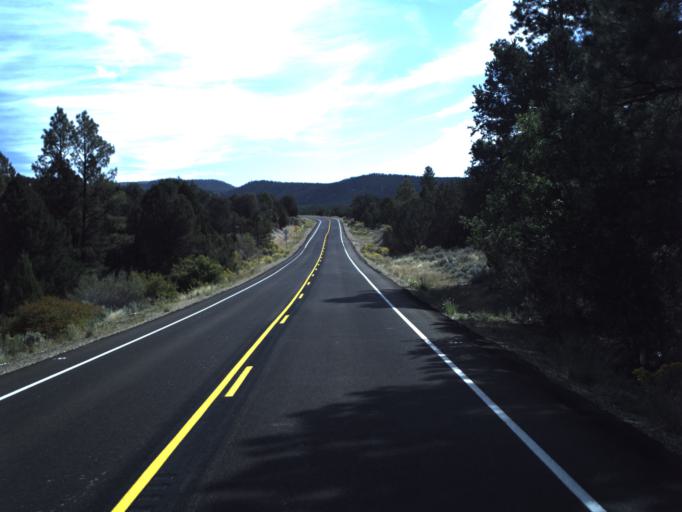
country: US
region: Utah
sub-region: Garfield County
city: Panguitch
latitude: 37.6165
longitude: -111.8916
